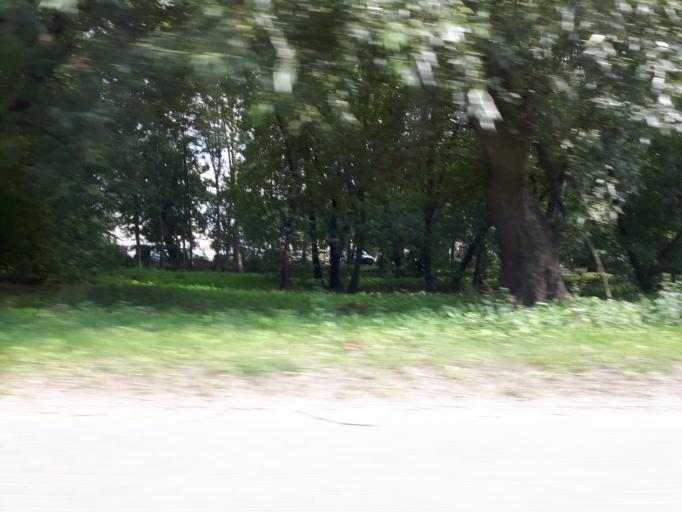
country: PL
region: Masovian Voivodeship
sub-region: Warszawa
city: Praga Poludnie
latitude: 52.2689
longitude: 21.0758
